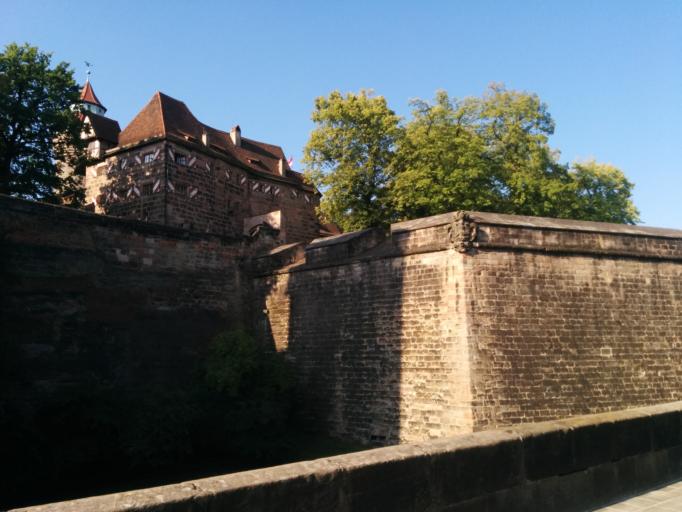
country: DE
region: Bavaria
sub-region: Regierungsbezirk Mittelfranken
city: Nuernberg
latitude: 49.4587
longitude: 11.0773
